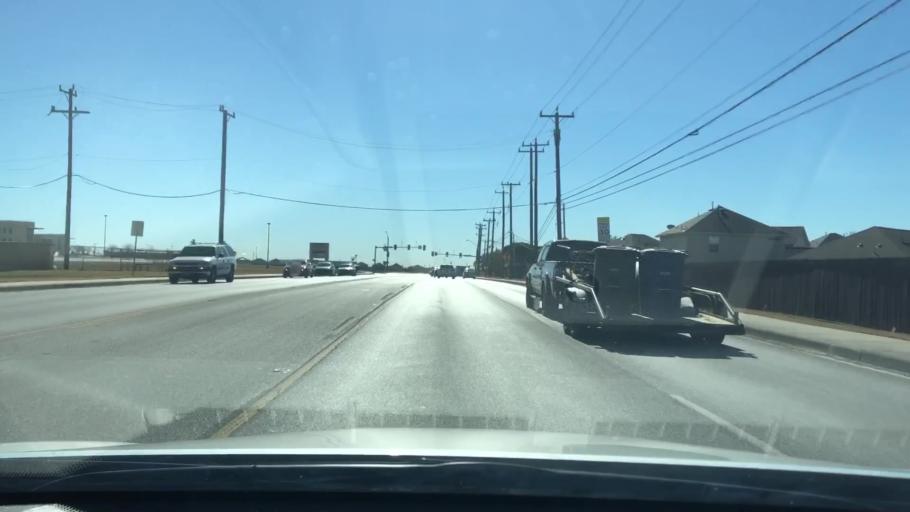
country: US
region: Texas
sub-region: Bexar County
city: Kirby
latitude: 29.4596
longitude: -98.3595
